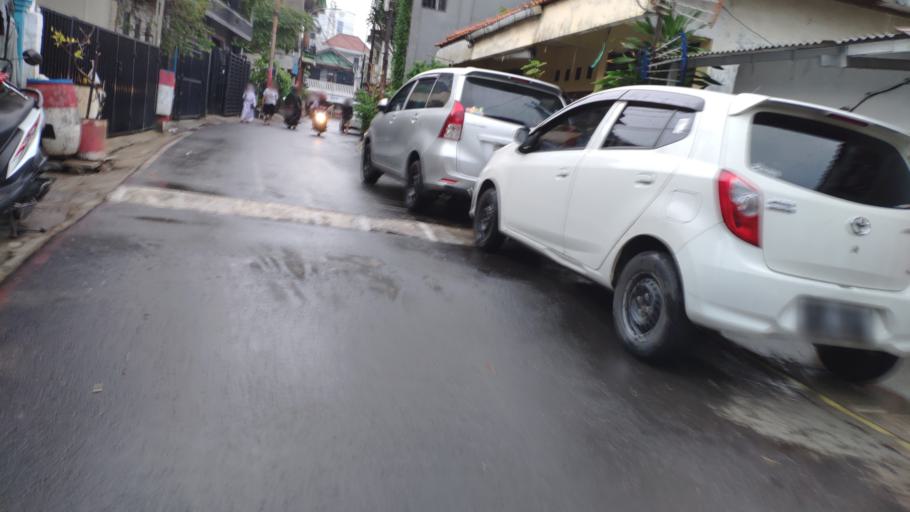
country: ID
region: Jakarta Raya
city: Jakarta
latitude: -6.2053
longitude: 106.8707
